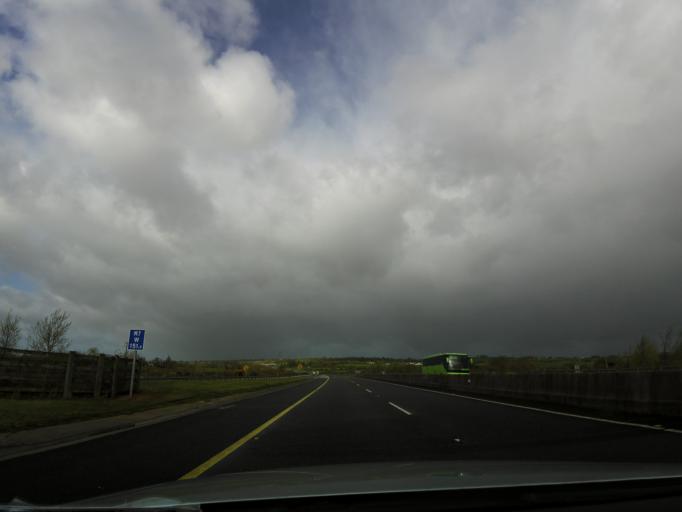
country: IE
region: Munster
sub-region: North Tipperary
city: Nenagh
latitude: 52.8452
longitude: -8.2522
